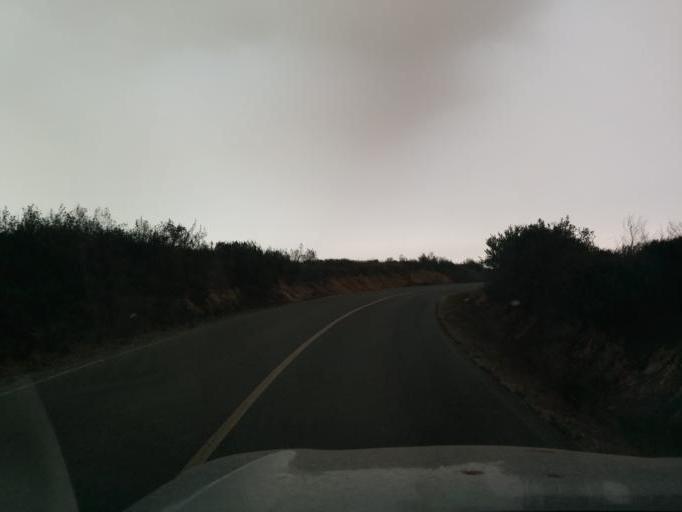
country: PT
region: Beja
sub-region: Odemira
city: Sao Teotonio
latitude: 37.5483
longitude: -8.7443
